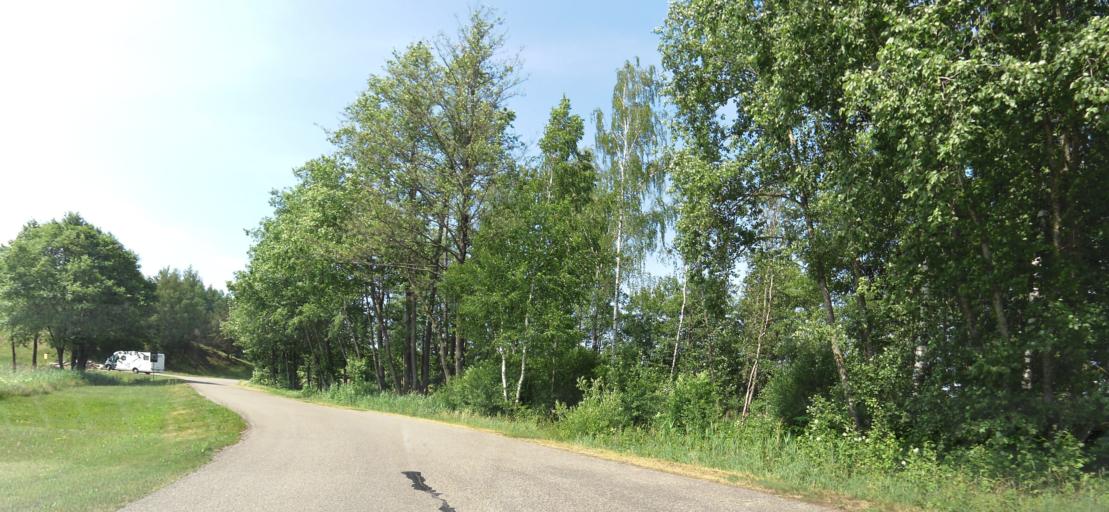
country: LT
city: Nemencine
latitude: 54.9086
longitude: 25.3216
